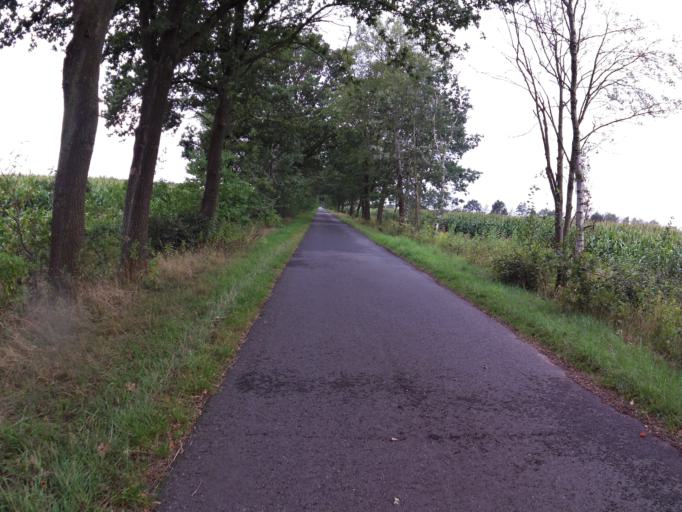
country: DE
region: Lower Saxony
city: Rotenburg
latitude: 53.1434
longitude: 9.4420
